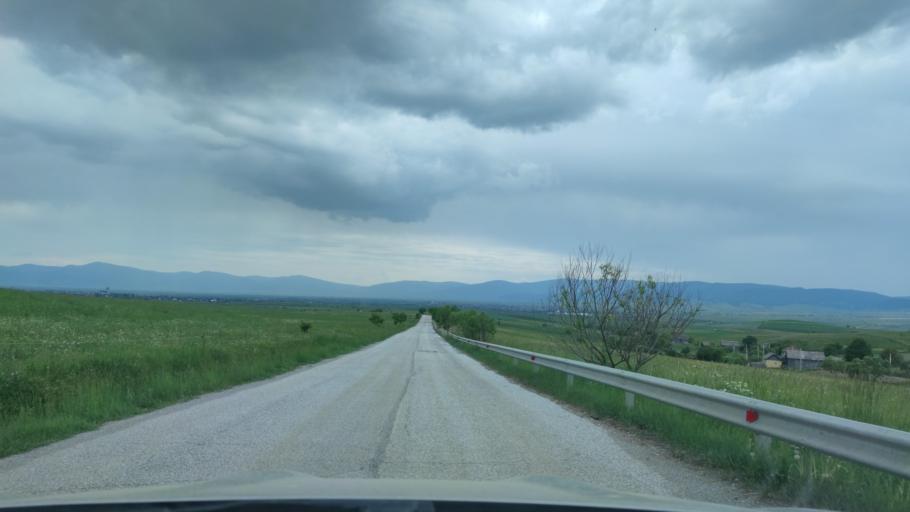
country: RO
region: Harghita
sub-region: Comuna Ditrau
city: Ditrau
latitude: 46.8447
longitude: 25.5004
